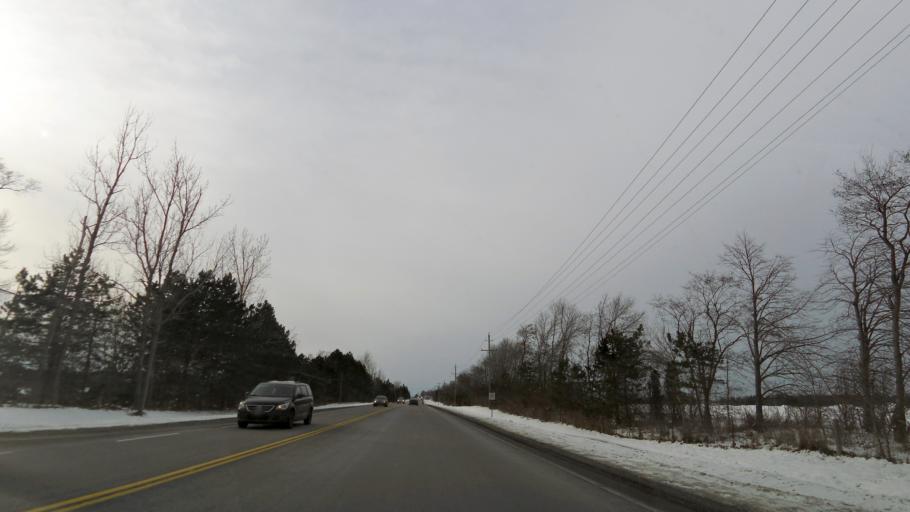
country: CA
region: Ontario
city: Ancaster
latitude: 43.2952
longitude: -79.9850
